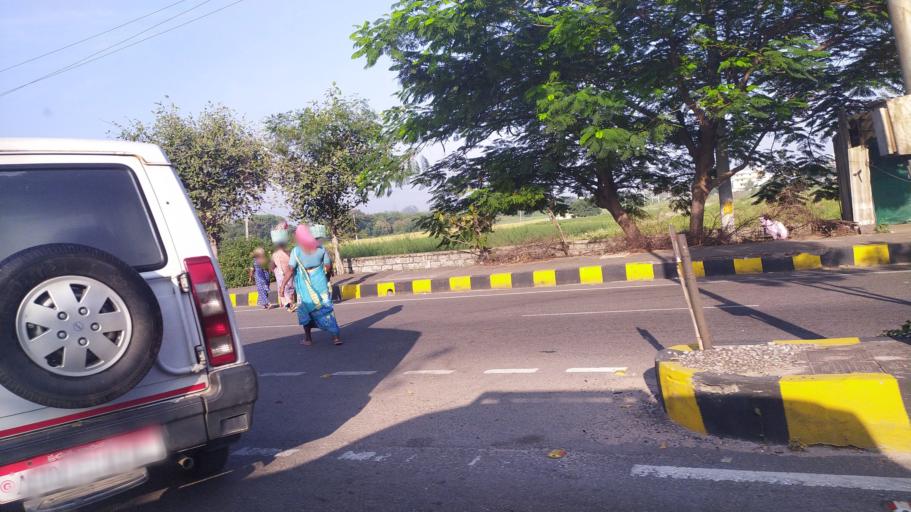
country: IN
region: Telangana
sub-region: Hyderabad
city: Hyderabad
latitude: 17.3263
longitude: 78.4082
